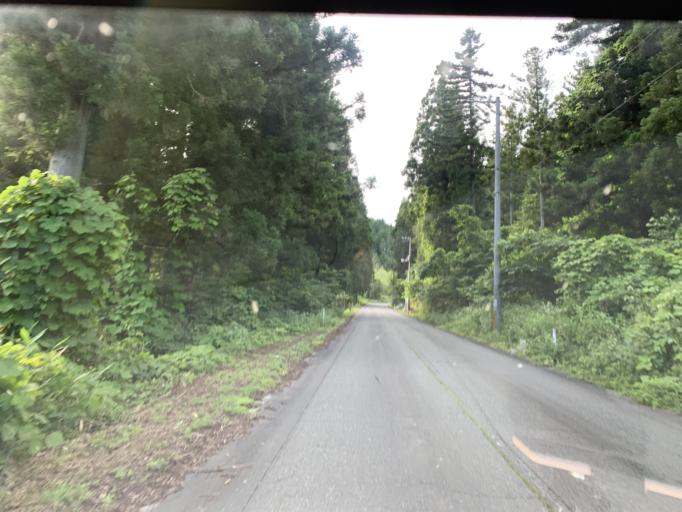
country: JP
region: Iwate
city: Ichinoseki
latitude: 38.8898
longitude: 140.9821
